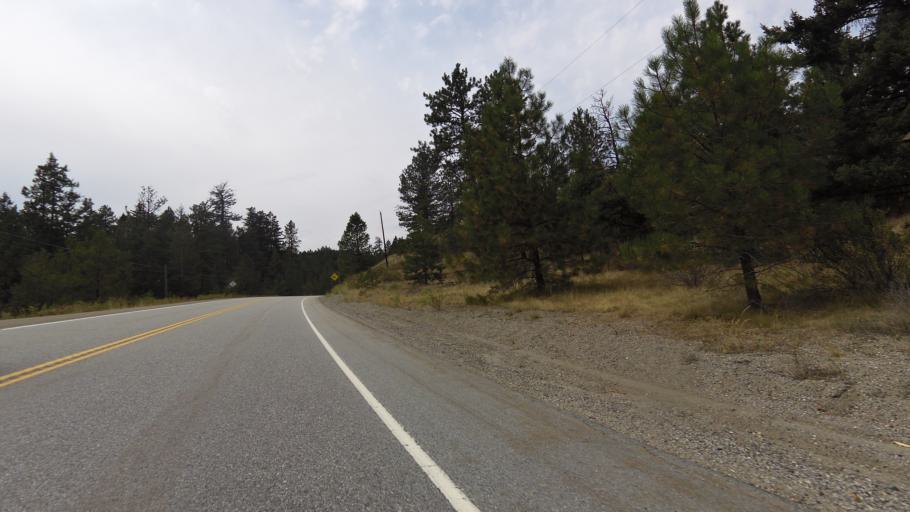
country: US
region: Washington
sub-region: Okanogan County
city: Oroville
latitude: 49.0043
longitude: -119.3181
